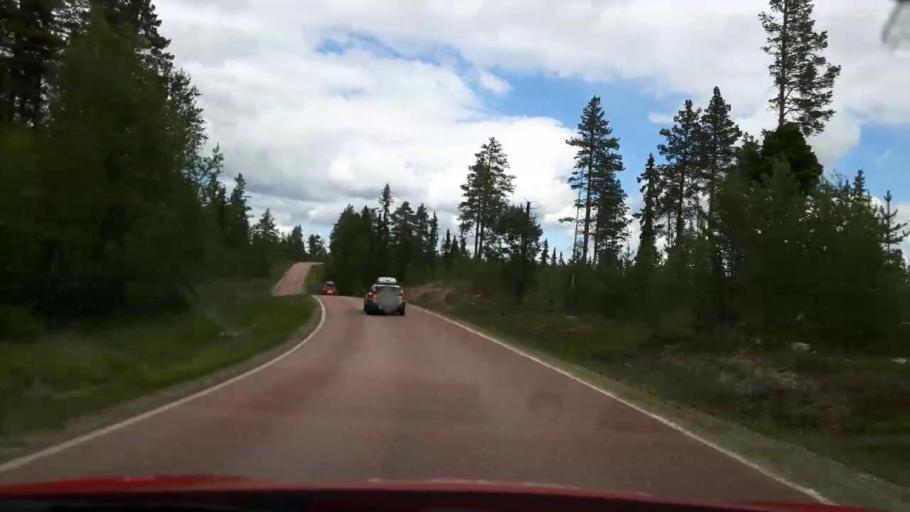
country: NO
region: Hedmark
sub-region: Trysil
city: Innbygda
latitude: 61.8702
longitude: 12.9599
